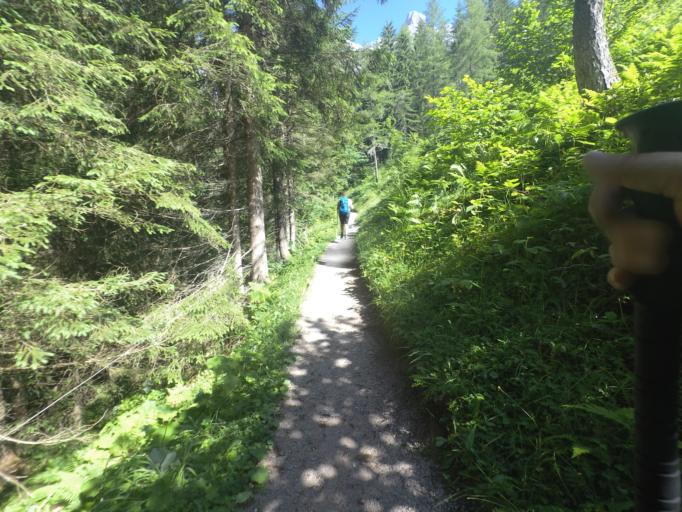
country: AT
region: Salzburg
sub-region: Politischer Bezirk Zell am See
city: Leogang
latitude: 47.4569
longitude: 12.7518
